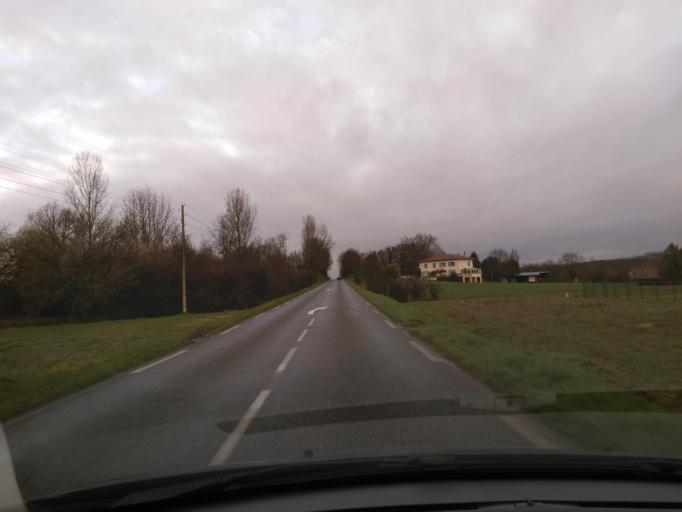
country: FR
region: Midi-Pyrenees
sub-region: Departement de la Haute-Garonne
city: Montesquieu-Volvestre
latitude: 43.1478
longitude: 1.3006
